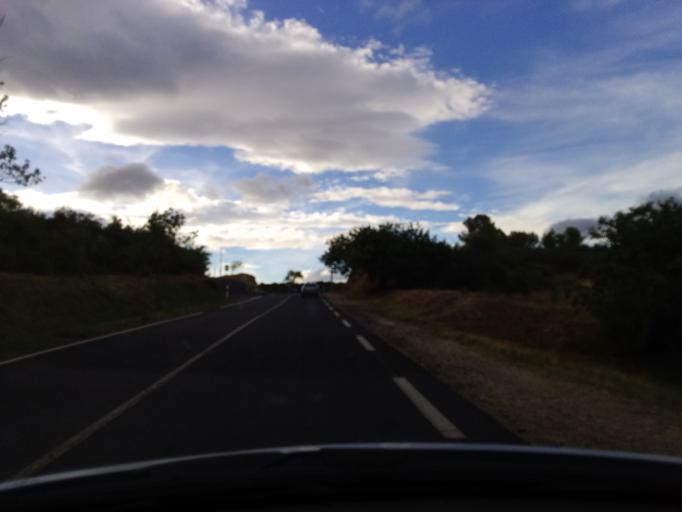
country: FR
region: Languedoc-Roussillon
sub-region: Departement de l'Herault
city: Nebian
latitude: 43.6399
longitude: 3.4182
